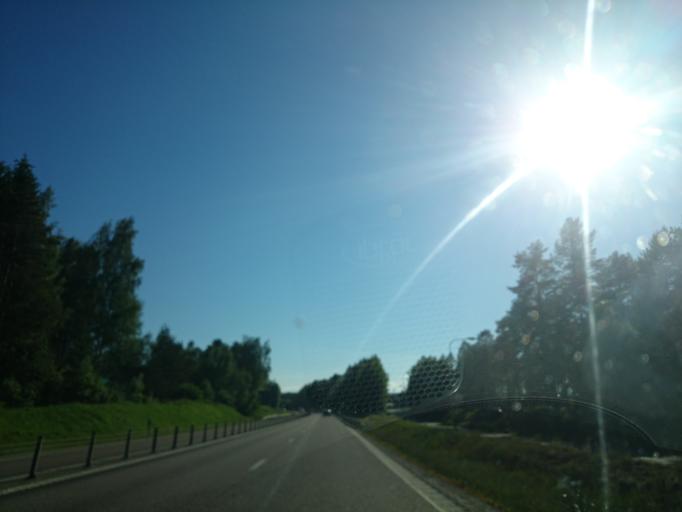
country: SE
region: Vaesternorrland
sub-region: Timra Kommun
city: Bergeforsen
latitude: 62.5138
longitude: 17.3745
